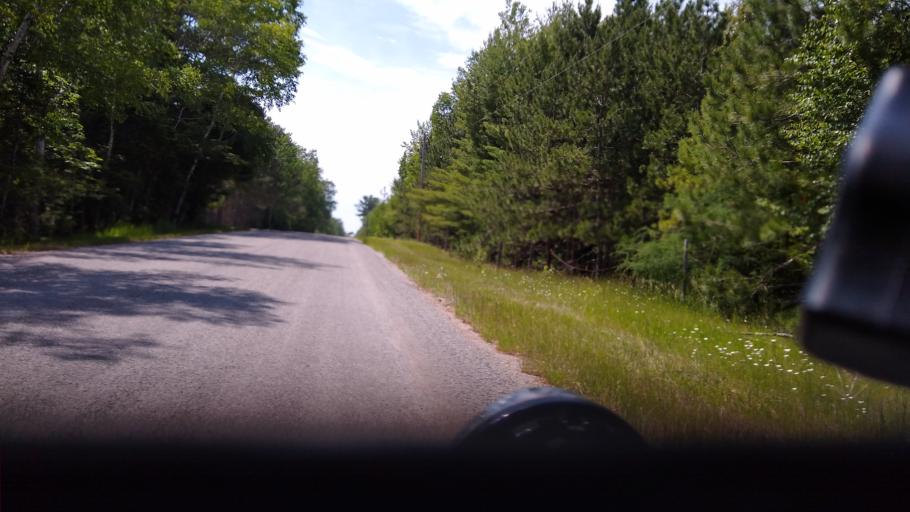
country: US
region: Michigan
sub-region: Delta County
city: Escanaba
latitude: 45.7099
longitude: -87.1489
